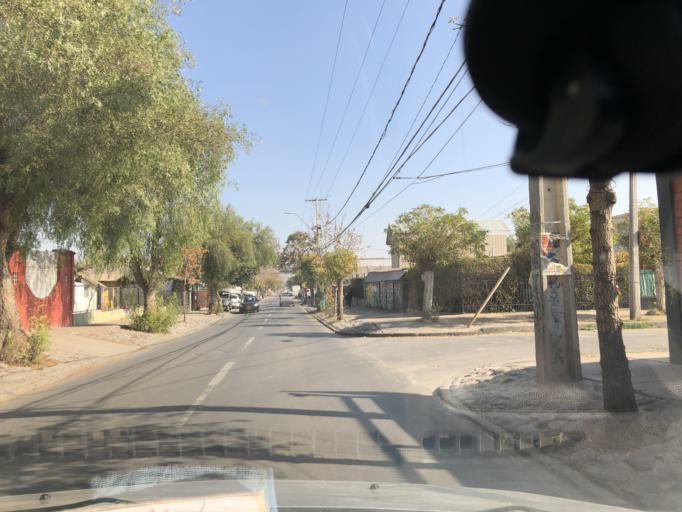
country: CL
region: Santiago Metropolitan
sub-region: Provincia de Cordillera
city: Puente Alto
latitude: -33.6225
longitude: -70.5794
